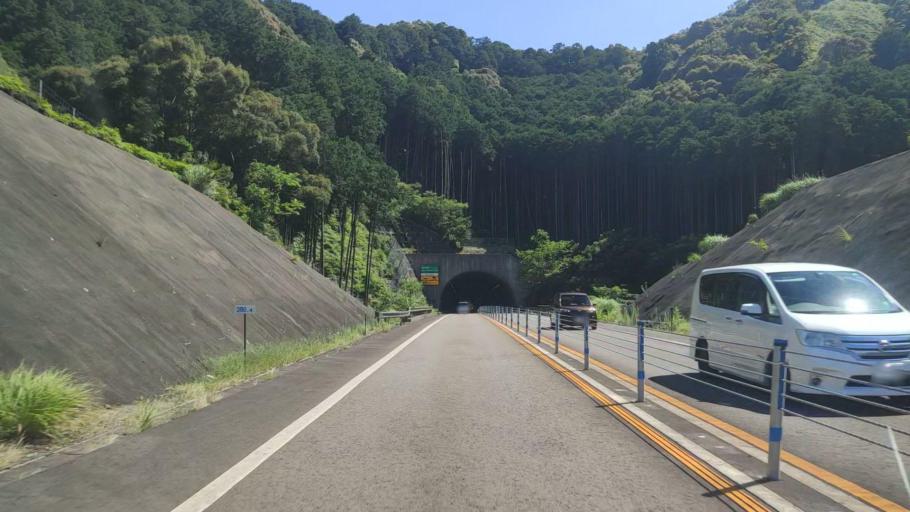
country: JP
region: Wakayama
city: Shingu
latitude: 33.6264
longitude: 135.9211
